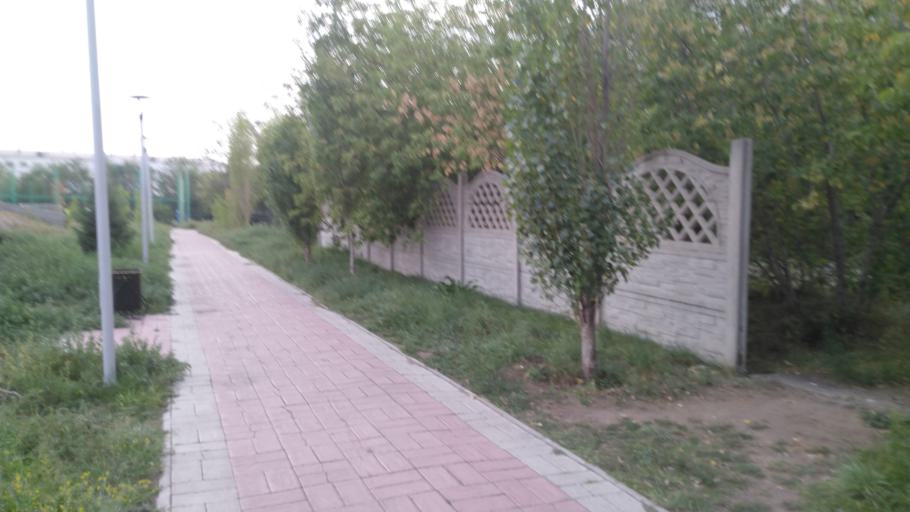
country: KZ
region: Pavlodar
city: Pavlodar
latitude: 52.3006
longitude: 76.9482
